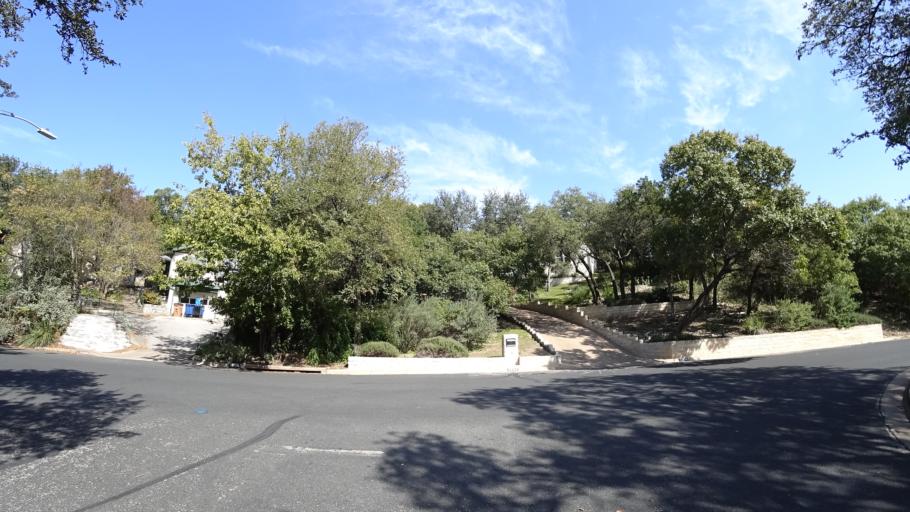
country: US
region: Texas
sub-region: Travis County
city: West Lake Hills
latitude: 30.3528
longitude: -97.7624
